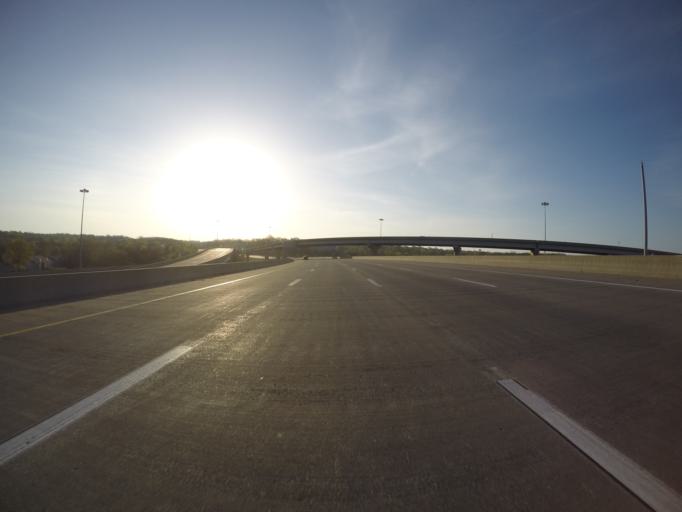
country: US
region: Missouri
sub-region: Jackson County
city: Grandview
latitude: 38.9329
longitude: -94.5286
